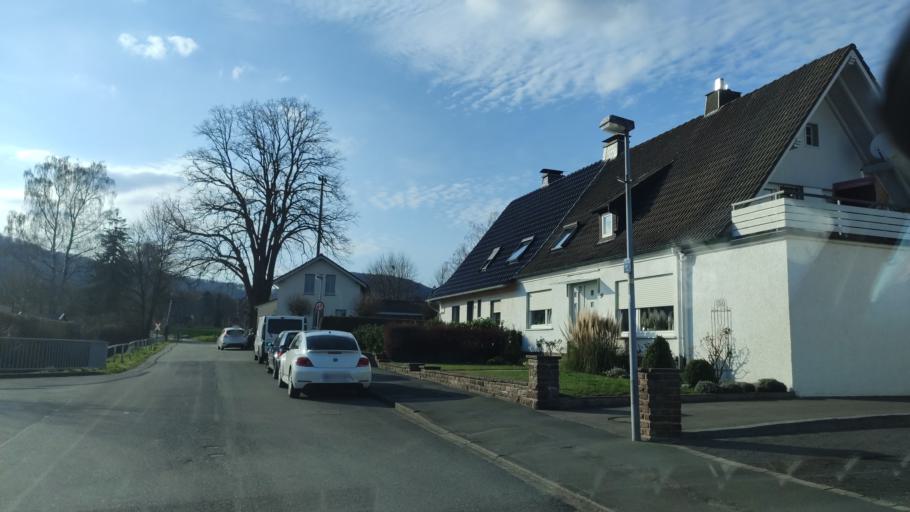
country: DE
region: Lower Saxony
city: Boffzen
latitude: 51.7346
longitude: 9.3579
